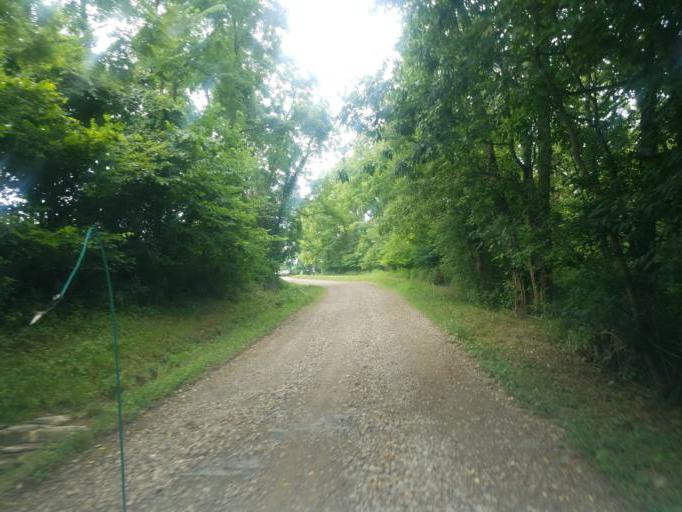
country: US
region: Ohio
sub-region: Knox County
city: Oak Hill
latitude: 40.3284
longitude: -82.1029
